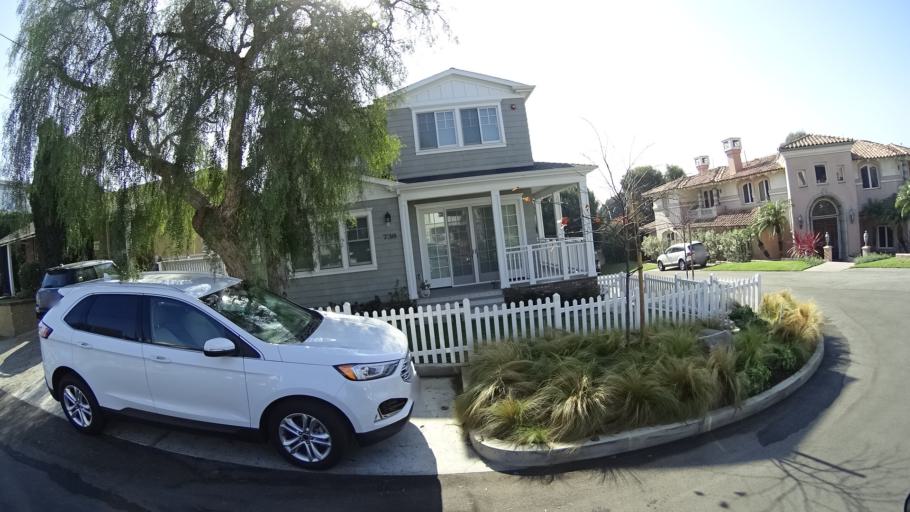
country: US
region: California
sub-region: Los Angeles County
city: Manhattan Beach
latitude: 33.8955
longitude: -118.4058
